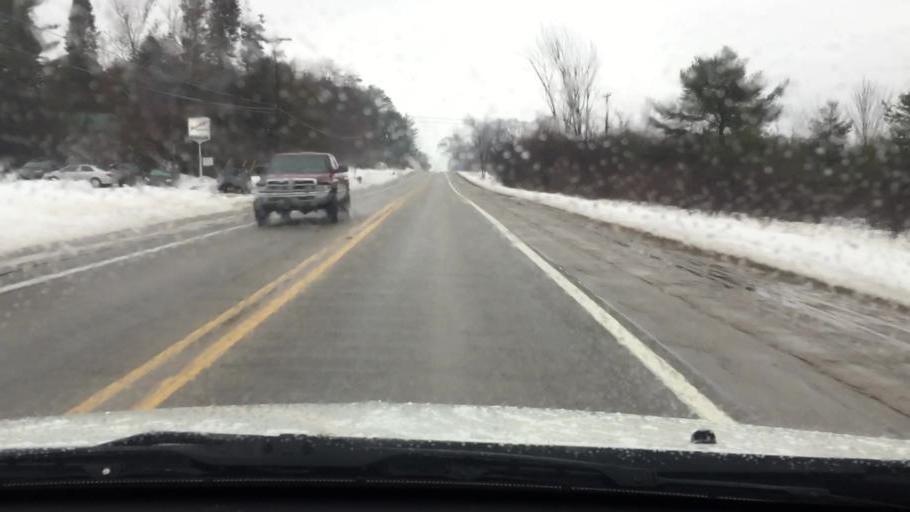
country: US
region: Michigan
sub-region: Charlevoix County
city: East Jordan
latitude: 45.1405
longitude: -85.1398
